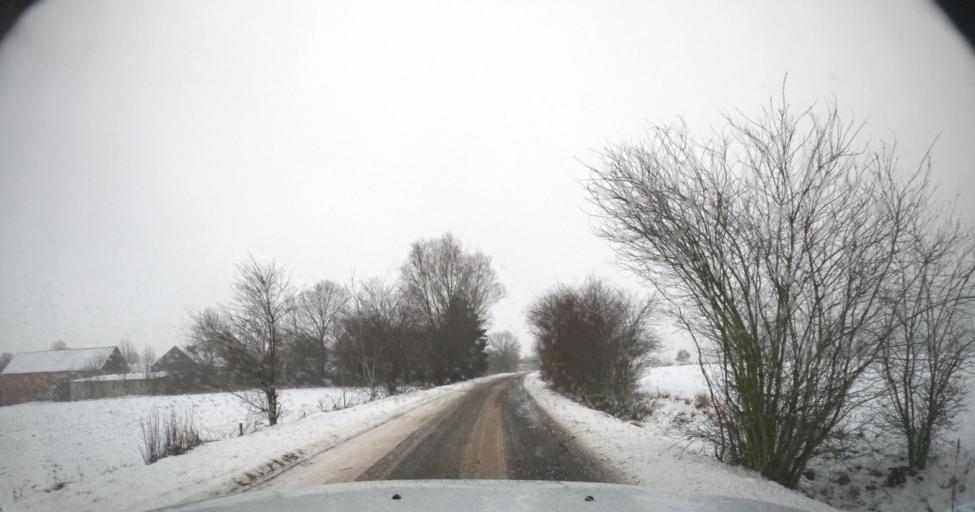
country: PL
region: West Pomeranian Voivodeship
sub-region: Powiat kamienski
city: Golczewo
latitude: 53.7930
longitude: 14.9641
